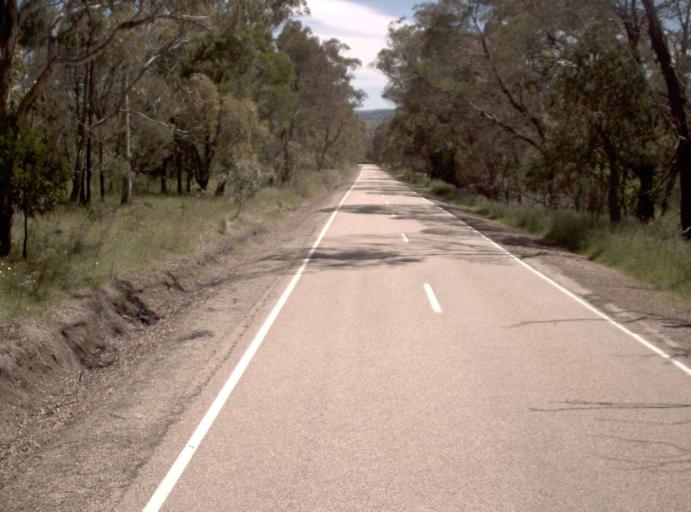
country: AU
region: Victoria
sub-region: East Gippsland
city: Lakes Entrance
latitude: -37.2772
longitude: 148.2553
